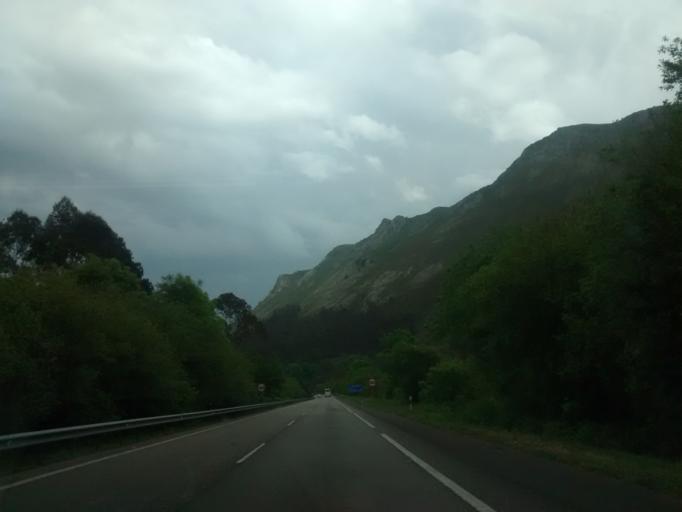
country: ES
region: Asturias
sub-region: Province of Asturias
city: Ribadesella
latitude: 43.4353
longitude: -5.0032
